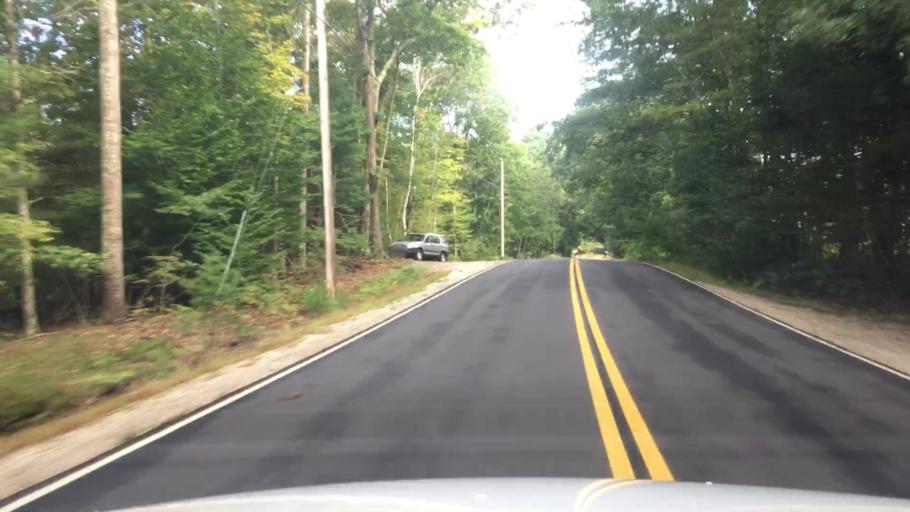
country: US
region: Maine
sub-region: York County
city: York Harbor
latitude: 43.1127
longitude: -70.6700
